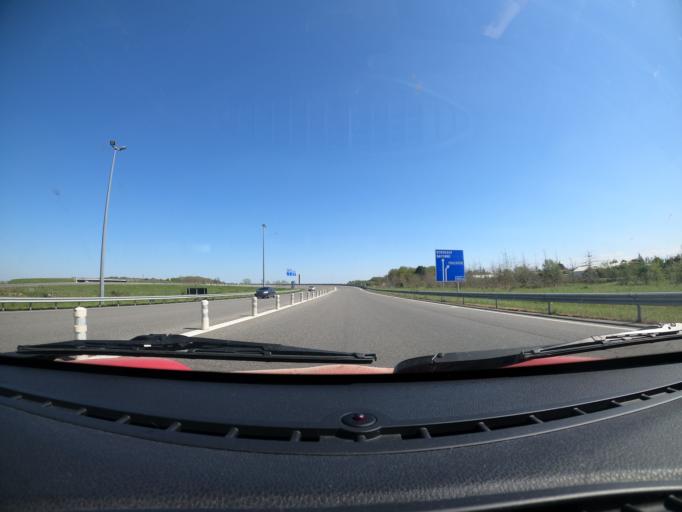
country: FR
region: Aquitaine
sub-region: Departement des Pyrenees-Atlantiques
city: Lescar
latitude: 43.3449
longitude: -0.4177
